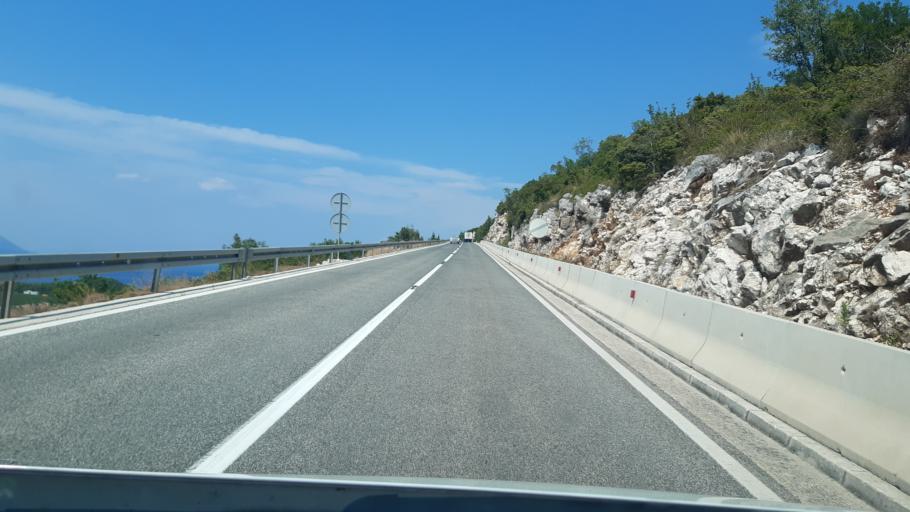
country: HR
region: Dubrovacko-Neretvanska
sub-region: Grad Dubrovnik
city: Opuzen
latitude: 42.9596
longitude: 17.5238
